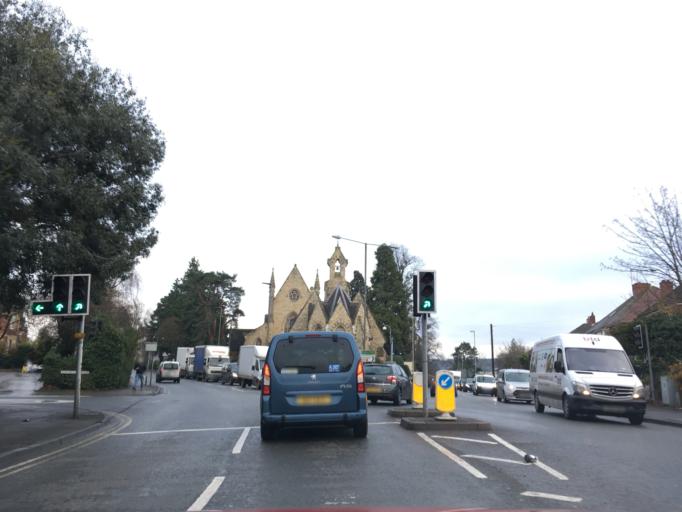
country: GB
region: England
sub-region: Gloucestershire
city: Charlton Kings
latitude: 51.8906
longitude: -2.0603
